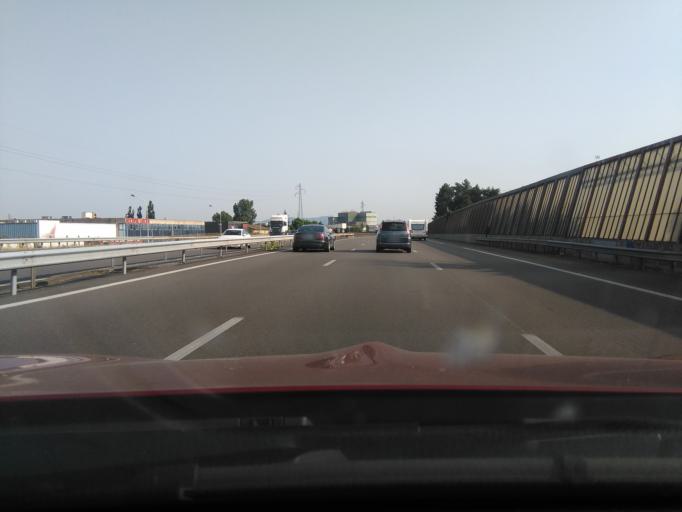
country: FR
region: Rhone-Alpes
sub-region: Departement du Rhone
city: Villefranche-sur-Saone
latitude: 45.9947
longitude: 4.7364
